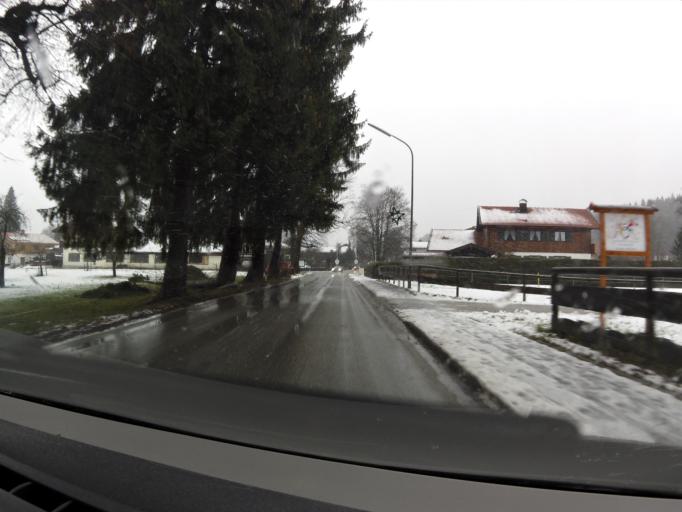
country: DE
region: Bavaria
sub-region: Upper Bavaria
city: Gmund am Tegernsee
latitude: 47.7540
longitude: 11.7166
